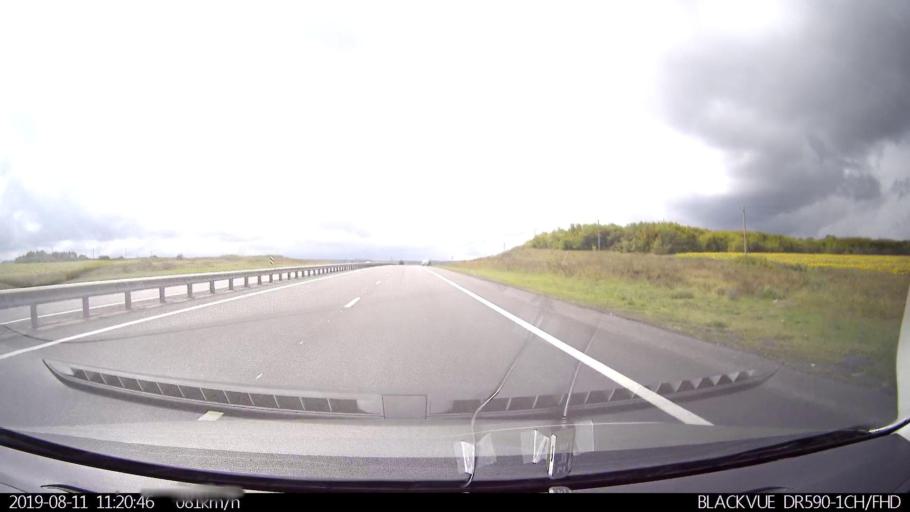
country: RU
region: Ulyanovsk
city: Novoul'yanovsk
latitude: 54.1541
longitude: 48.2644
